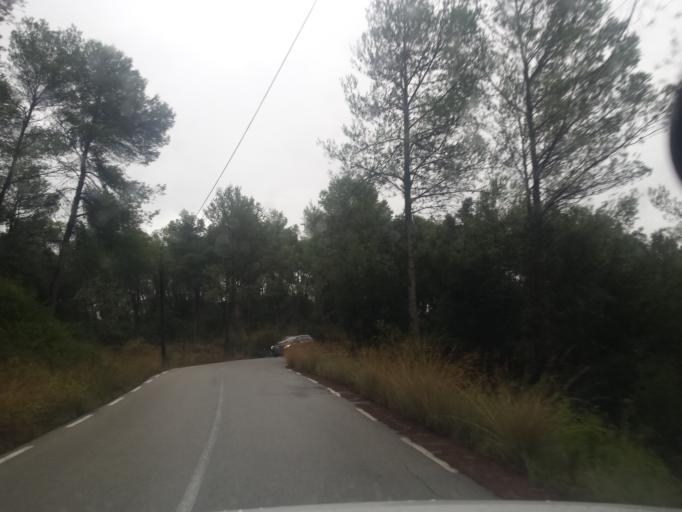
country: ES
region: Catalonia
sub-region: Provincia de Barcelona
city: Sant Andreu de la Barca
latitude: 41.4358
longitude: 1.9442
